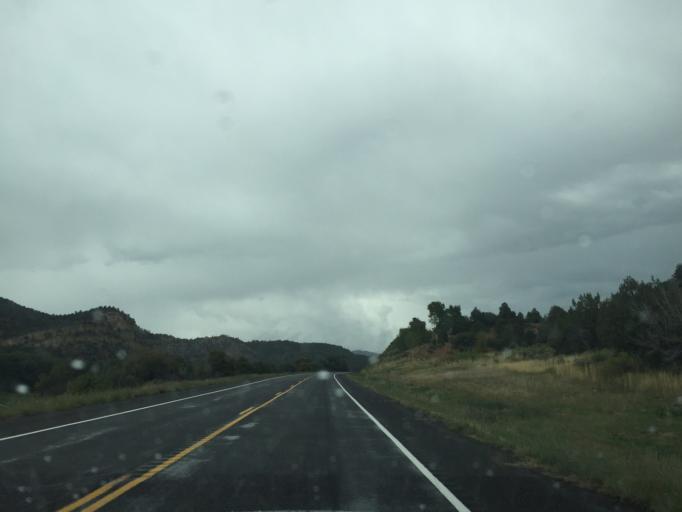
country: US
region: Utah
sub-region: Kane County
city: Kanab
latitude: 37.2893
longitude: -112.6197
